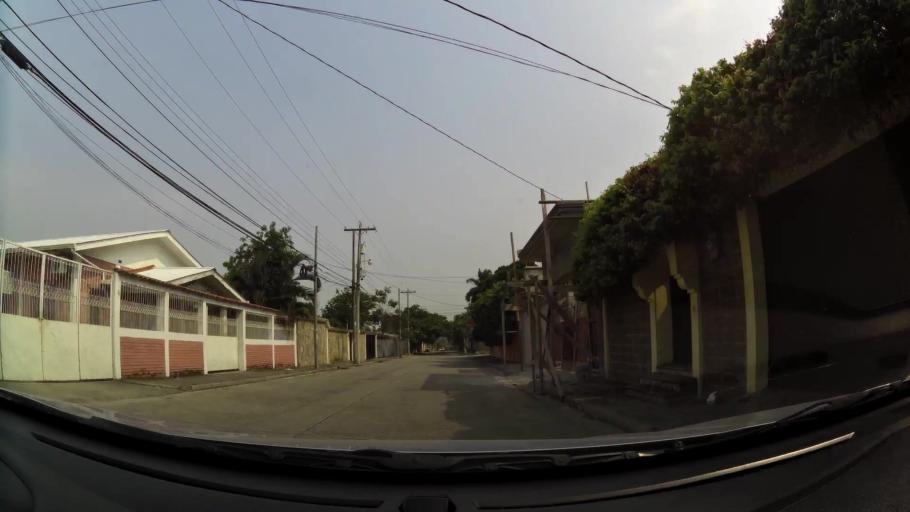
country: HN
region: Cortes
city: Armenta
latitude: 15.4974
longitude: -88.0424
